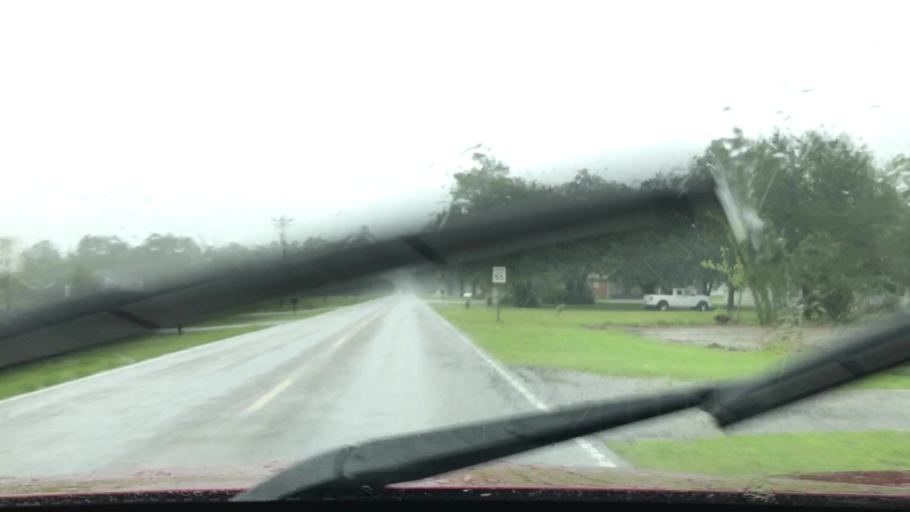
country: US
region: South Carolina
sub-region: Horry County
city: Red Hill
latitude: 33.8802
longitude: -78.9683
